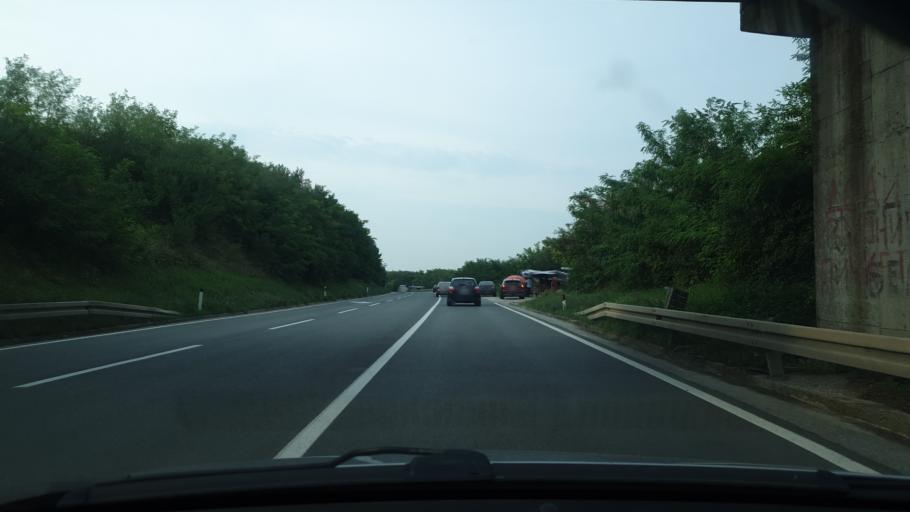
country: RS
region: Central Serbia
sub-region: Belgrade
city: Sopot
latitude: 44.5384
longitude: 20.6583
